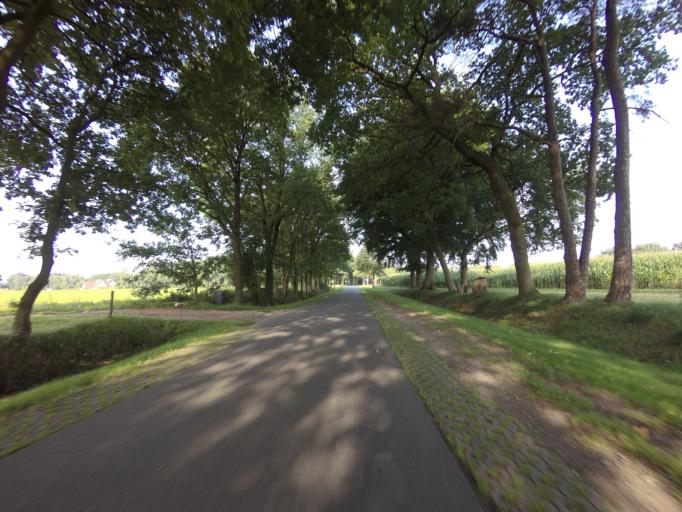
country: DE
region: Lower Saxony
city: Itterbeck
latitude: 52.4910
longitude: 6.8078
